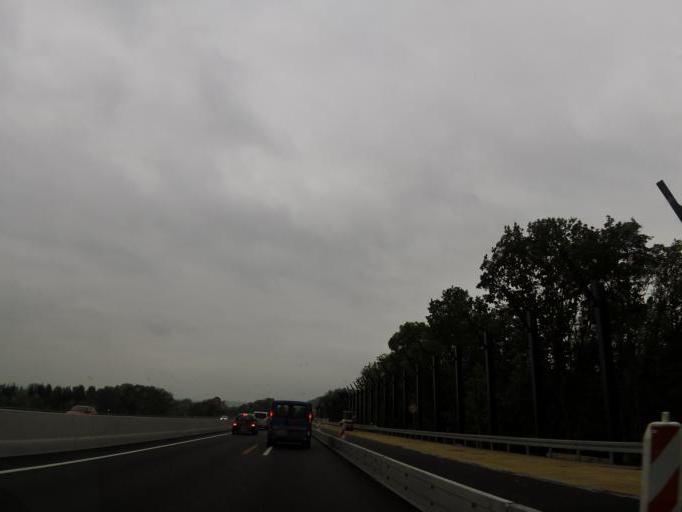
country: DE
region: Lower Saxony
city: Seesen
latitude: 51.8903
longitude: 10.1312
